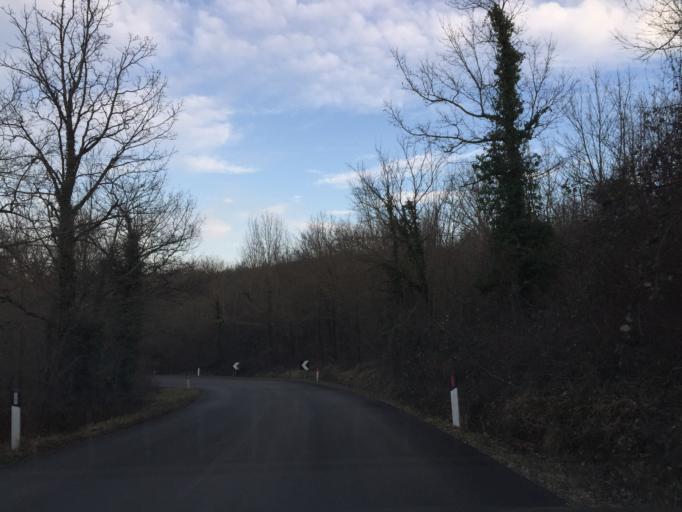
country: IT
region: Molise
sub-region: Provincia di Campobasso
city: Guardiaregia
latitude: 41.4478
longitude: 14.5531
